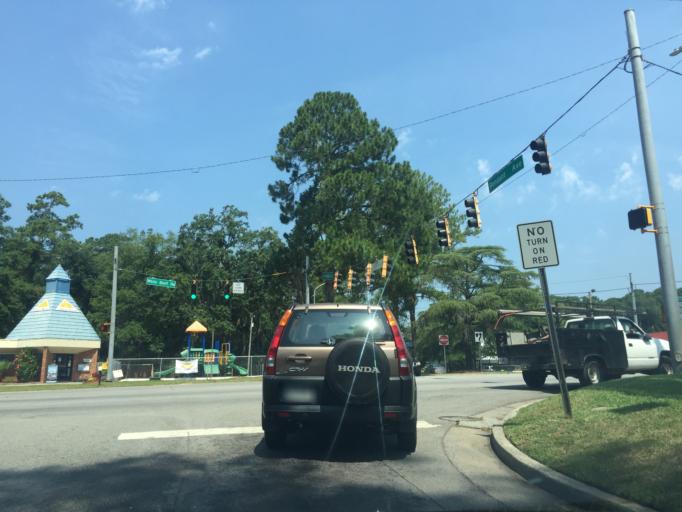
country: US
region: Georgia
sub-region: Chatham County
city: Montgomery
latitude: 31.9728
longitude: -81.1328
